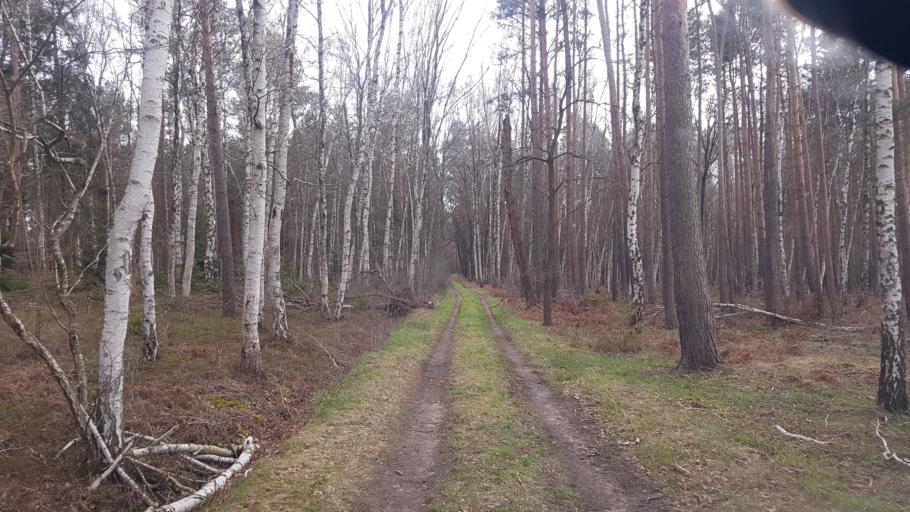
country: DE
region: Brandenburg
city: Hohenbucko
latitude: 51.6849
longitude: 13.4669
